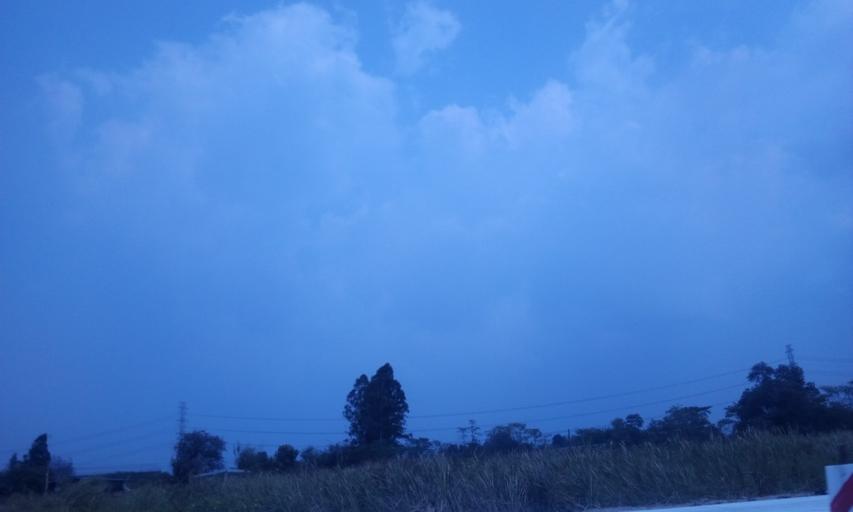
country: TH
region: Chon Buri
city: Ban Bueng
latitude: 13.3316
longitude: 101.1880
